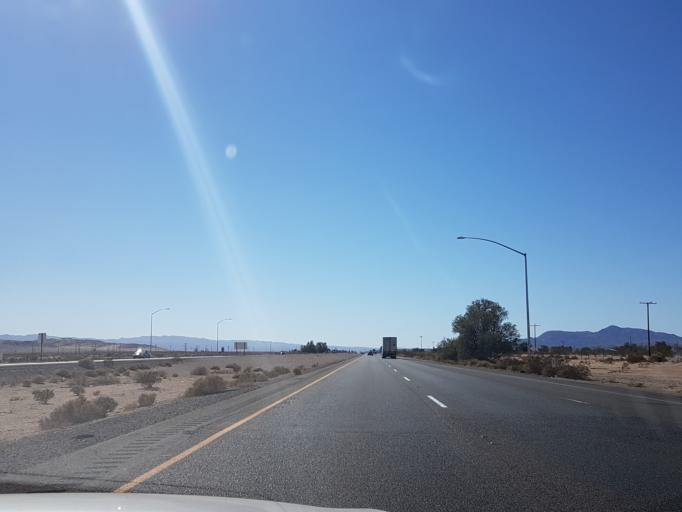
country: US
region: California
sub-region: San Bernardino County
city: Fort Irwin
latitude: 34.9623
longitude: -116.6480
